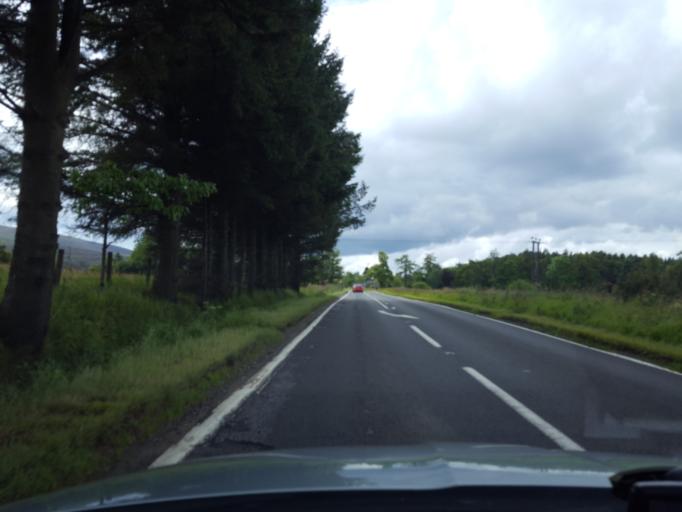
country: GB
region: Scotland
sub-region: Moray
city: Rothes
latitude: 57.4540
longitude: -3.2535
